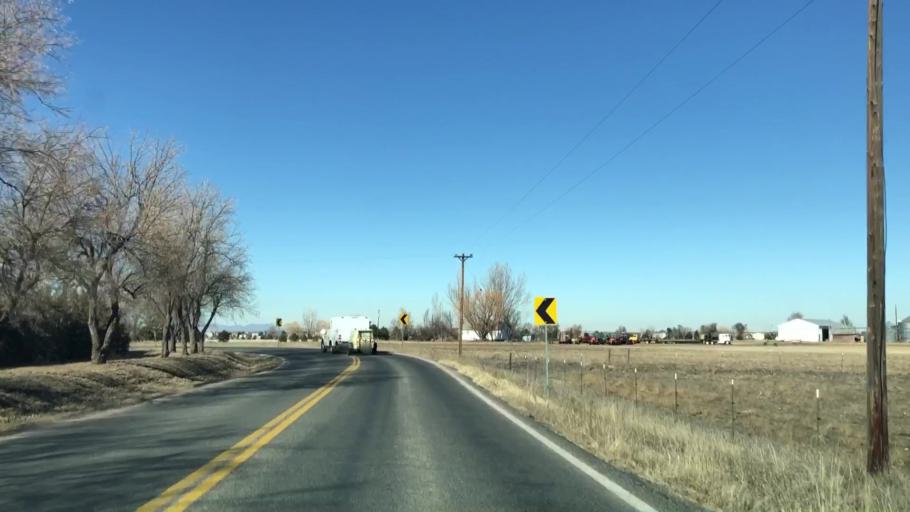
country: US
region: Colorado
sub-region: Weld County
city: Windsor
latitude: 40.4896
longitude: -104.9424
